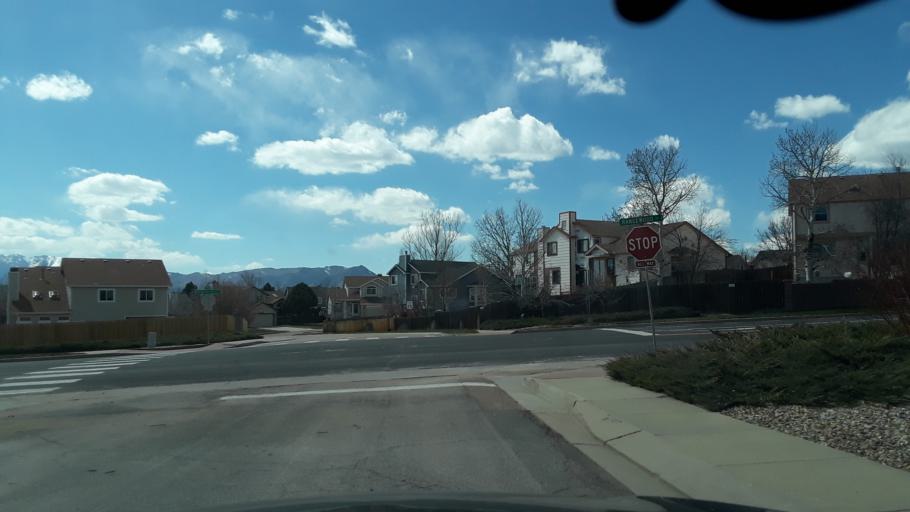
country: US
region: Colorado
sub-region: El Paso County
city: Black Forest
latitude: 38.9605
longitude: -104.7504
